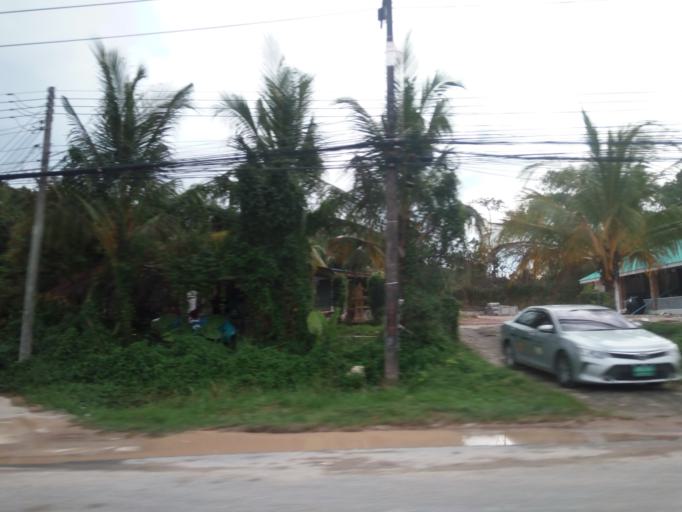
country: TH
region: Phuket
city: Thalang
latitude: 8.0955
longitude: 98.3100
